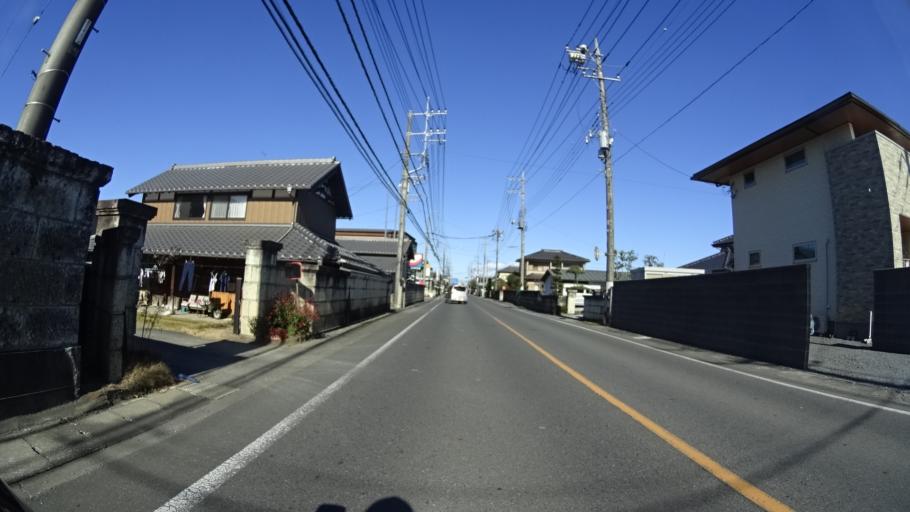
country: JP
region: Tochigi
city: Mibu
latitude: 36.4397
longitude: 139.7520
